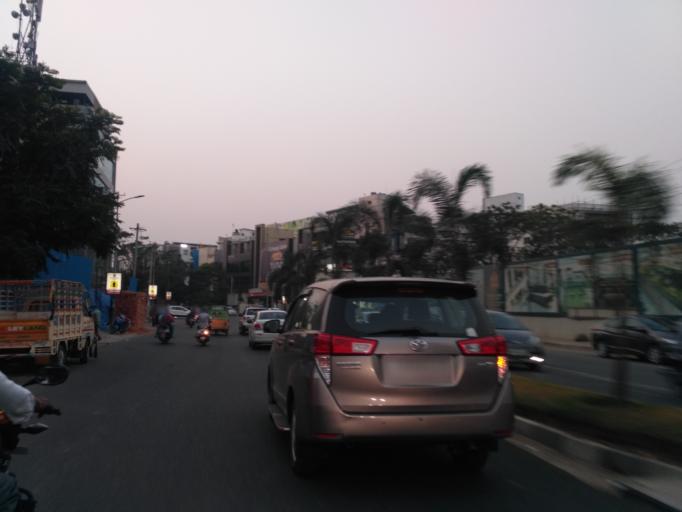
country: IN
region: Telangana
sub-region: Rangareddi
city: Kukatpalli
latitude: 17.4410
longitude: 78.3976
